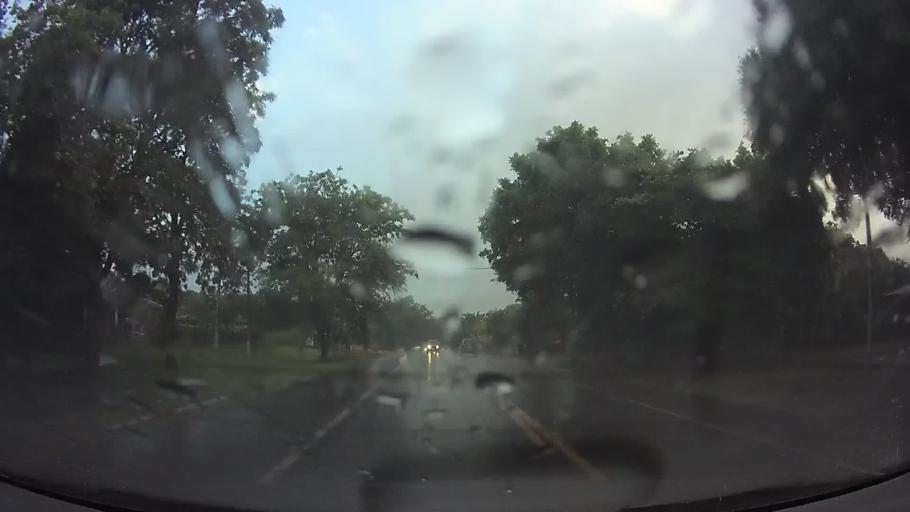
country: PY
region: Paraguari
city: Yaguaron
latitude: -25.5851
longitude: -57.2425
